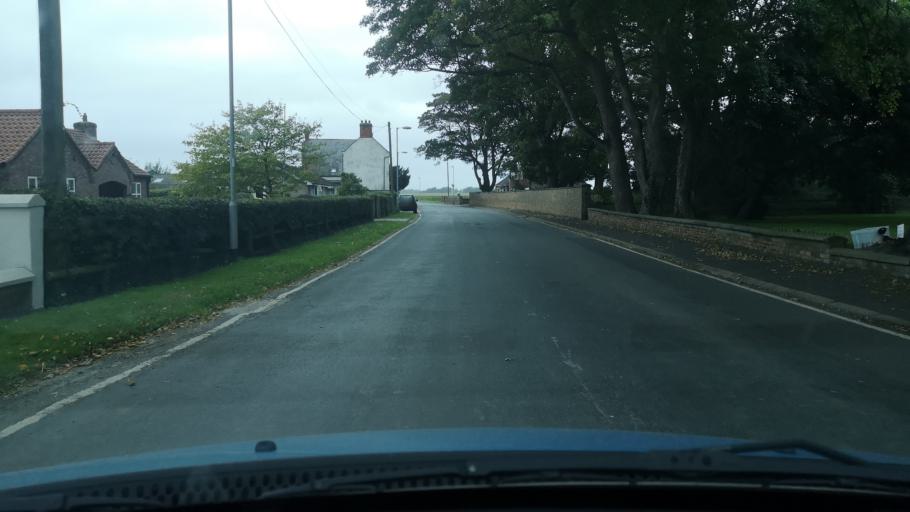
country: GB
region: England
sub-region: East Riding of Yorkshire
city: Laxton
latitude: 53.6997
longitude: -0.8008
